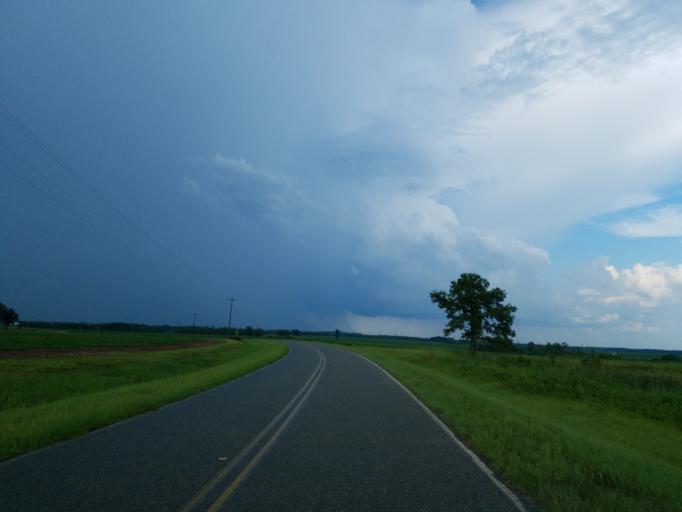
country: US
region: Georgia
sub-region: Cook County
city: Adel
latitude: 31.0676
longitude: -83.4456
